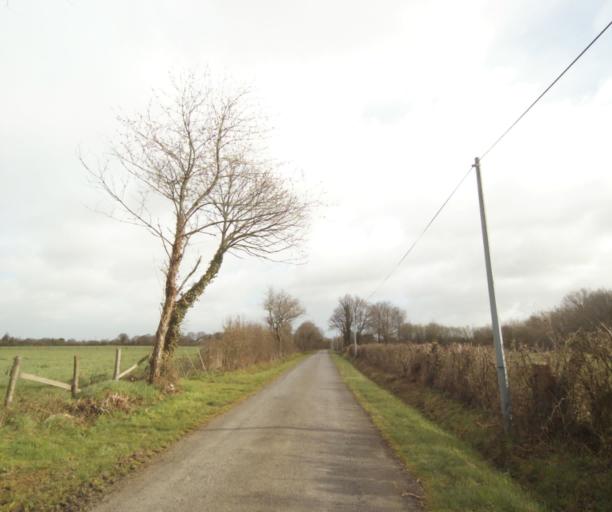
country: FR
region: Pays de la Loire
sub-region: Departement de la Loire-Atlantique
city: Bouvron
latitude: 47.3985
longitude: -1.8606
